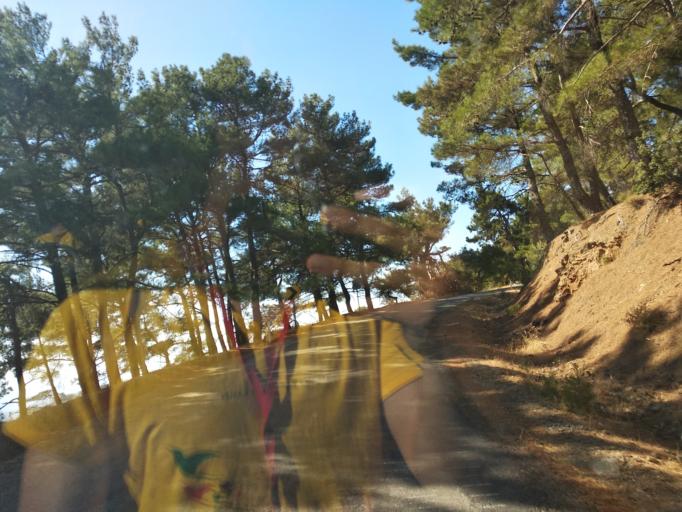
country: TR
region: Izmir
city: Gaziemir
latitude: 38.3017
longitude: 26.9980
